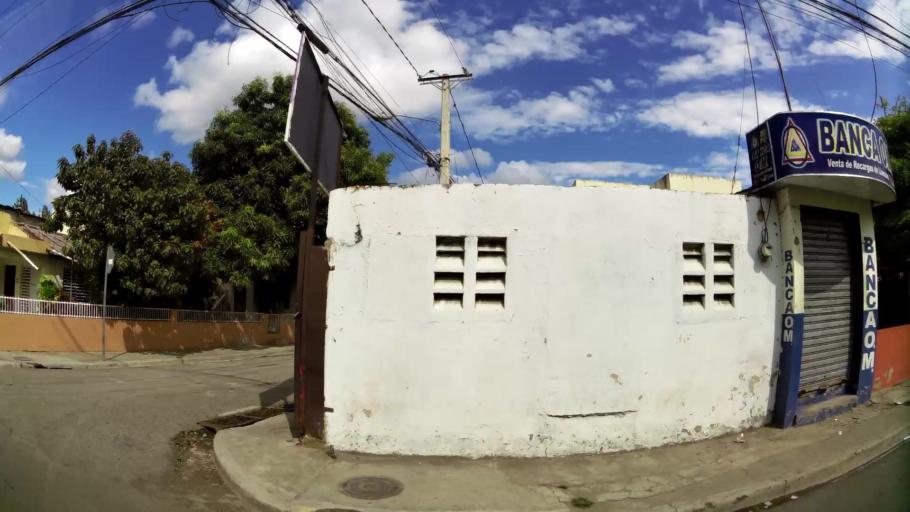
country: DO
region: La Vega
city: Concepcion de La Vega
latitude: 19.2267
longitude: -70.5253
